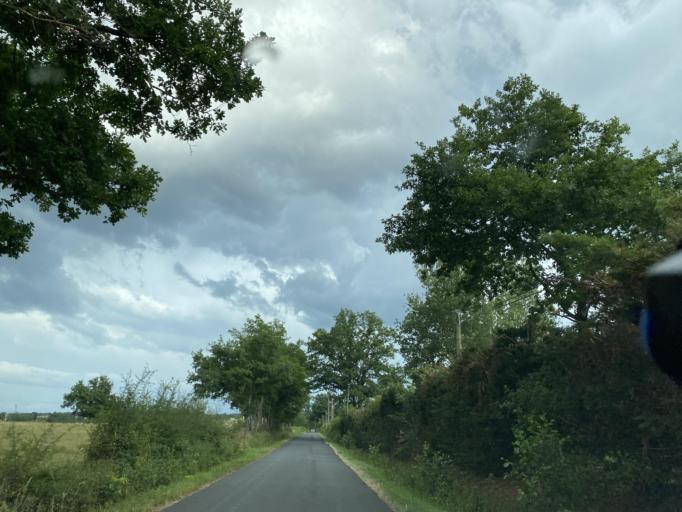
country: FR
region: Auvergne
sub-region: Departement du Puy-de-Dome
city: Peschadoires
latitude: 45.7765
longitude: 3.4404
